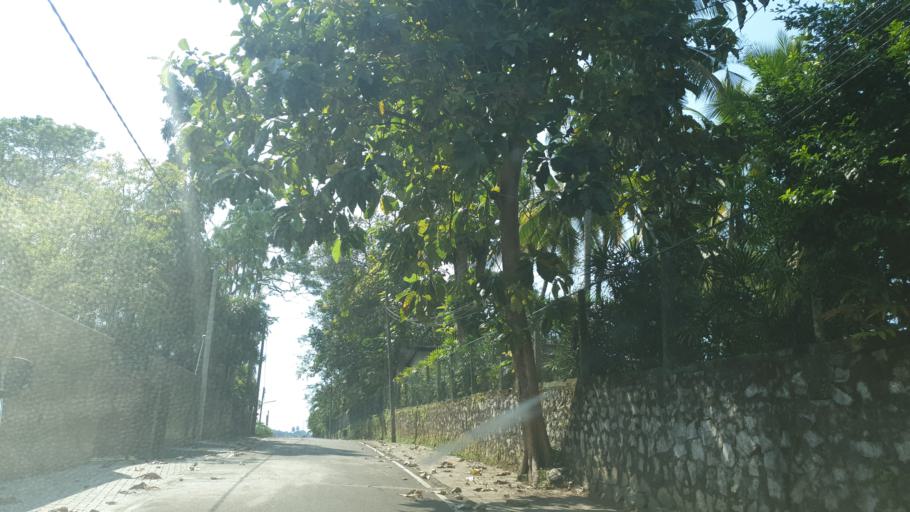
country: LK
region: Western
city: Moratuwa
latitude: 6.7596
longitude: 79.9223
